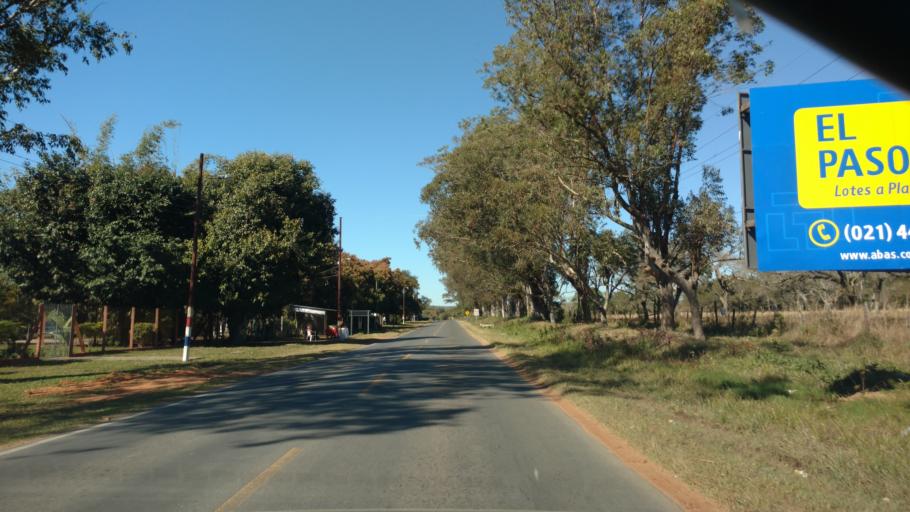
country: PY
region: Central
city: Ypacarai
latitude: -25.4426
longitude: -57.2768
